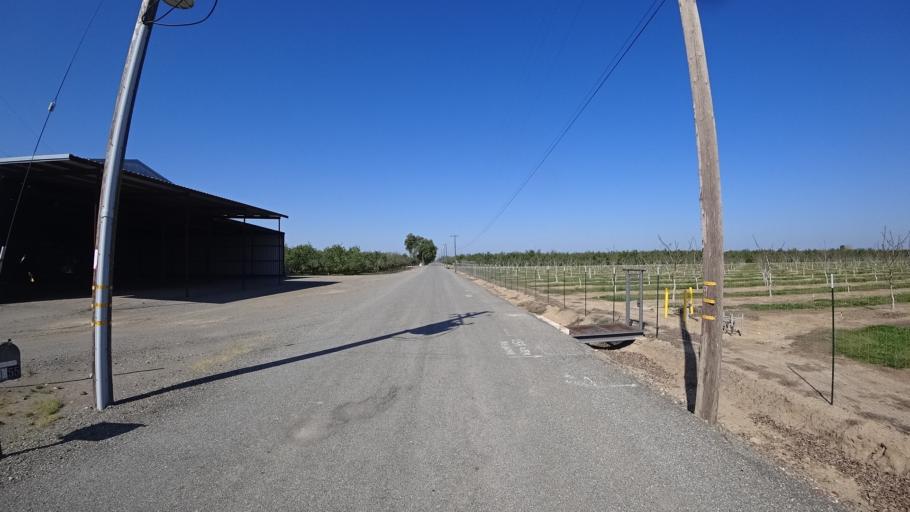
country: US
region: California
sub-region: Glenn County
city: Hamilton City
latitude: 39.6596
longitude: -122.0000
